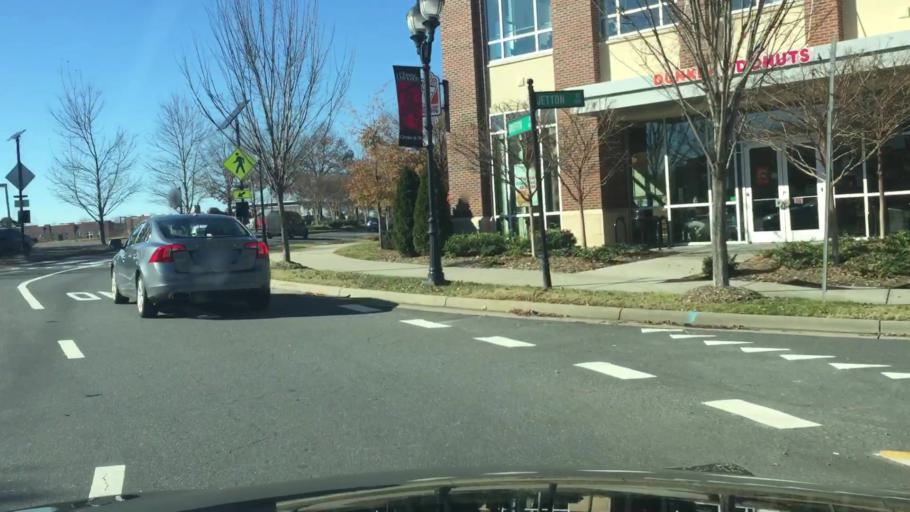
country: US
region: North Carolina
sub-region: Mecklenburg County
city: Cornelius
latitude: 35.5024
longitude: -80.8613
